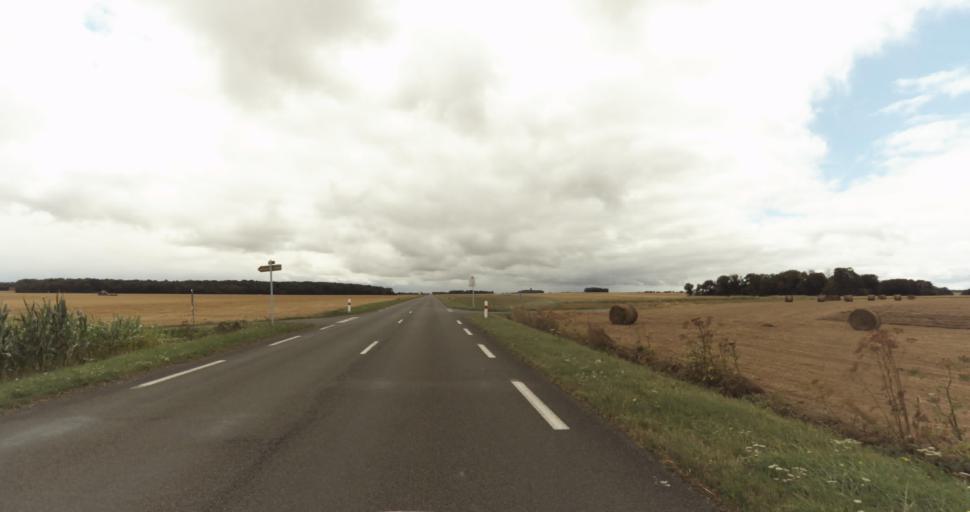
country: FR
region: Haute-Normandie
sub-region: Departement de l'Eure
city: Arnieres-sur-Iton
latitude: 48.9466
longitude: 1.1633
